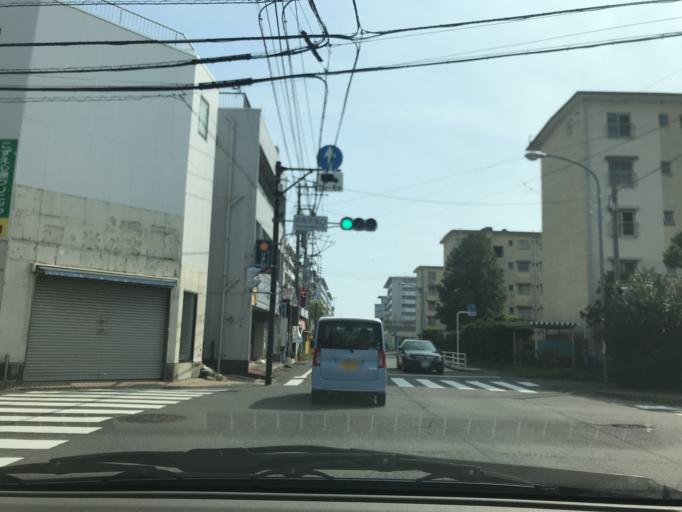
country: JP
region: Kanagawa
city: Chigasaki
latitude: 35.3273
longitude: 139.3886
